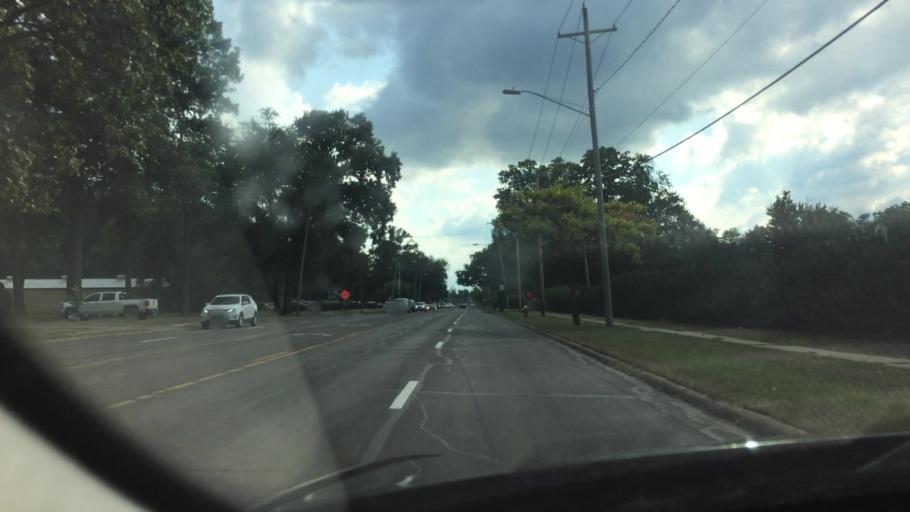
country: US
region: Ohio
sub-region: Lucas County
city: Maumee
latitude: 41.5982
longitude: -83.6347
